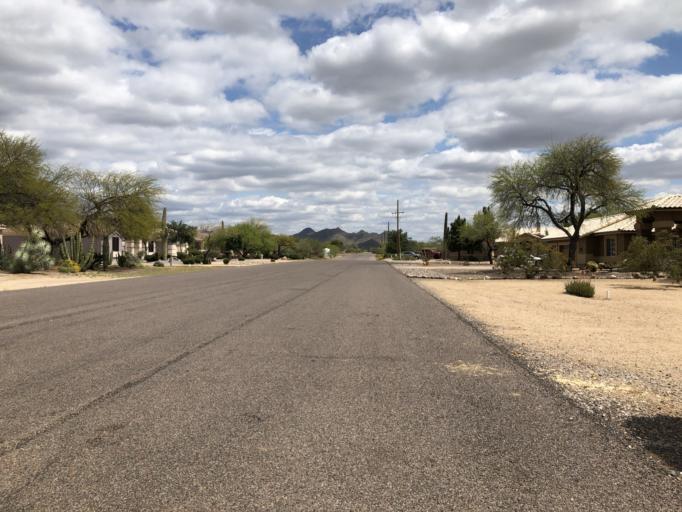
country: US
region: Arizona
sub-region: Maricopa County
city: Anthem
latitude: 33.8353
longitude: -112.0698
